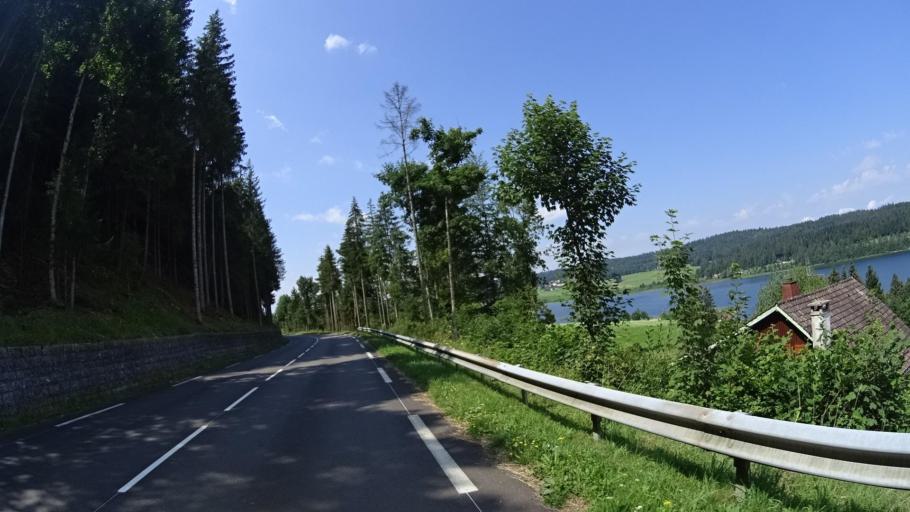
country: FR
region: Franche-Comte
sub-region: Departement du Doubs
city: Les Fourgs
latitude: 46.8297
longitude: 6.3385
